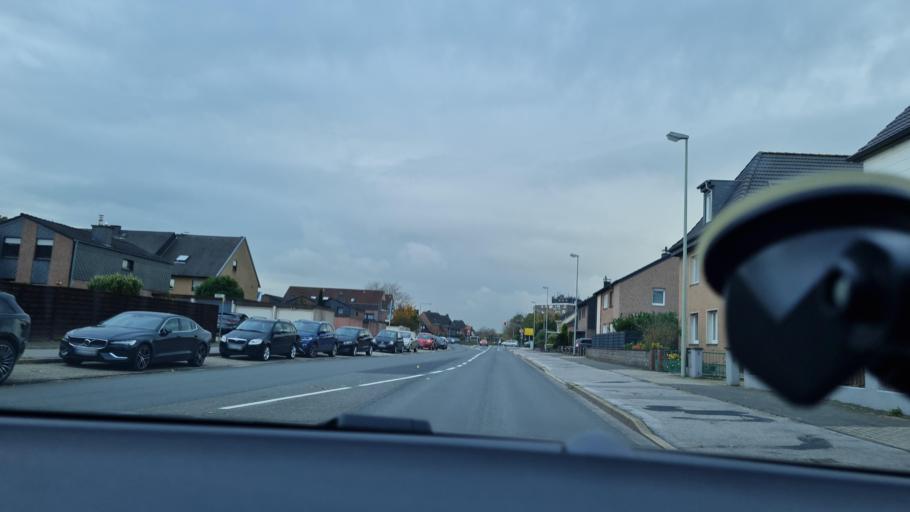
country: DE
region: North Rhine-Westphalia
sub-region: Regierungsbezirk Dusseldorf
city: Voerde
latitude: 51.6220
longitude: 6.6485
